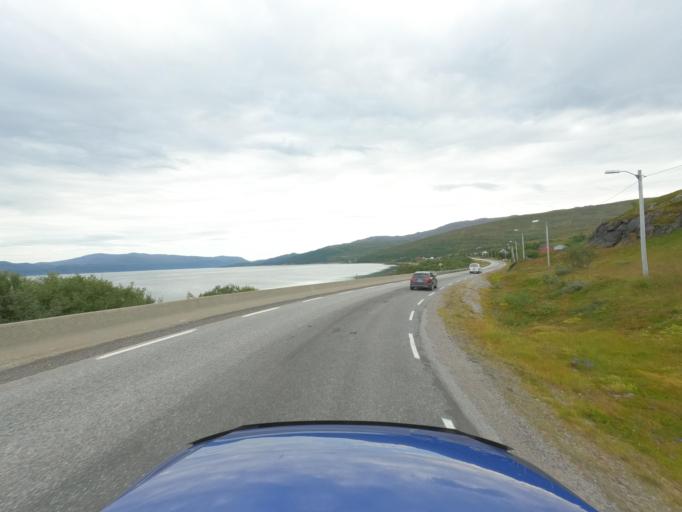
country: NO
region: Finnmark Fylke
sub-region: Kvalsund
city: Kvalsund
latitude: 70.5114
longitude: 24.0473
